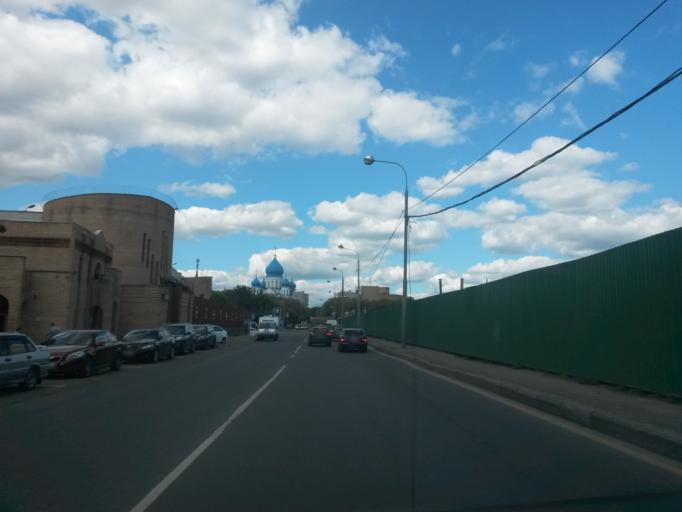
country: RU
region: Moscow
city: Mar'ino
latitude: 55.6649
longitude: 37.7201
